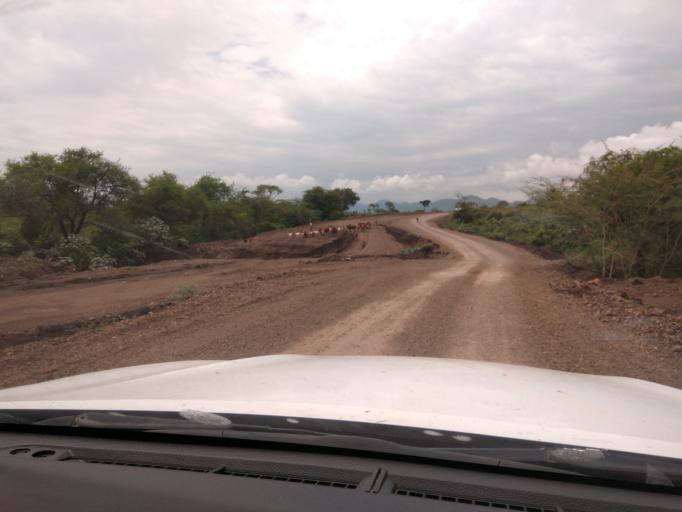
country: ET
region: Southern Nations, Nationalities, and People's Region
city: Felege Neway
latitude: 6.4036
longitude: 37.1320
